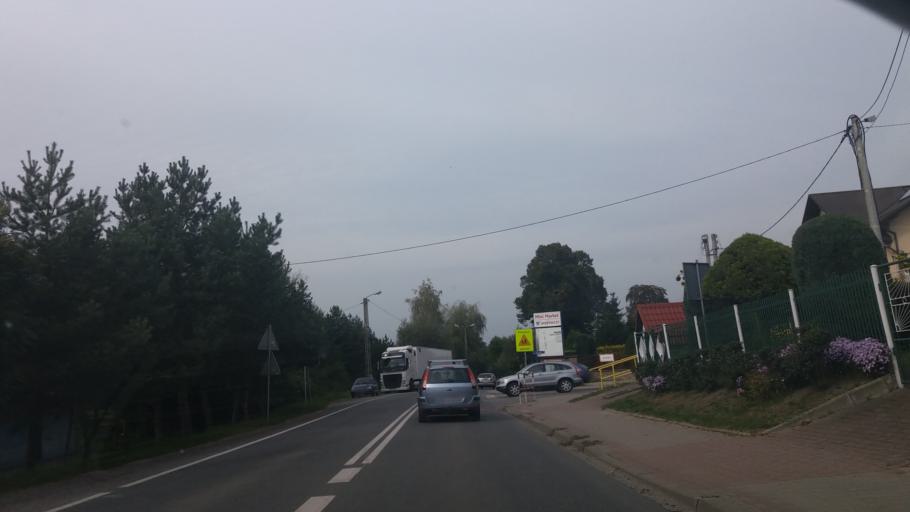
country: PL
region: Lesser Poland Voivodeship
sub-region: Powiat chrzanowski
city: Chrzanow
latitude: 50.1302
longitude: 19.4271
